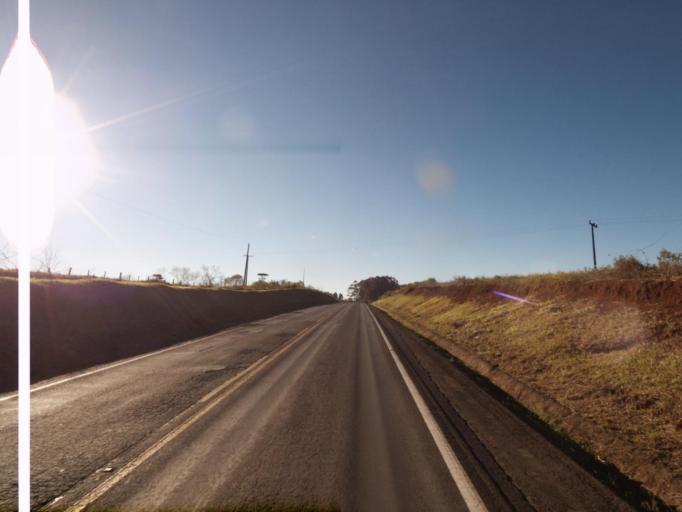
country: AR
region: Misiones
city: Bernardo de Irigoyen
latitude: -26.2935
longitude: -53.5549
